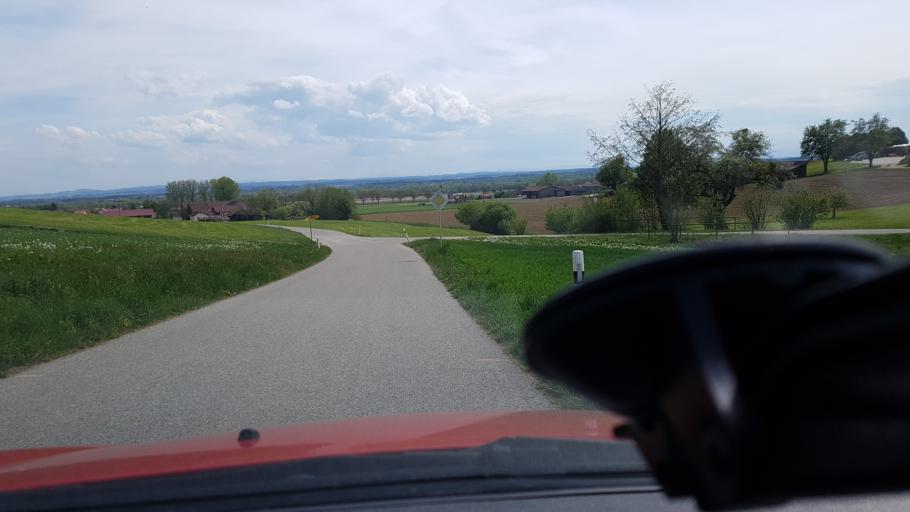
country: DE
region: Bavaria
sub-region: Lower Bavaria
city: Ering
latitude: 48.3092
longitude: 13.1258
